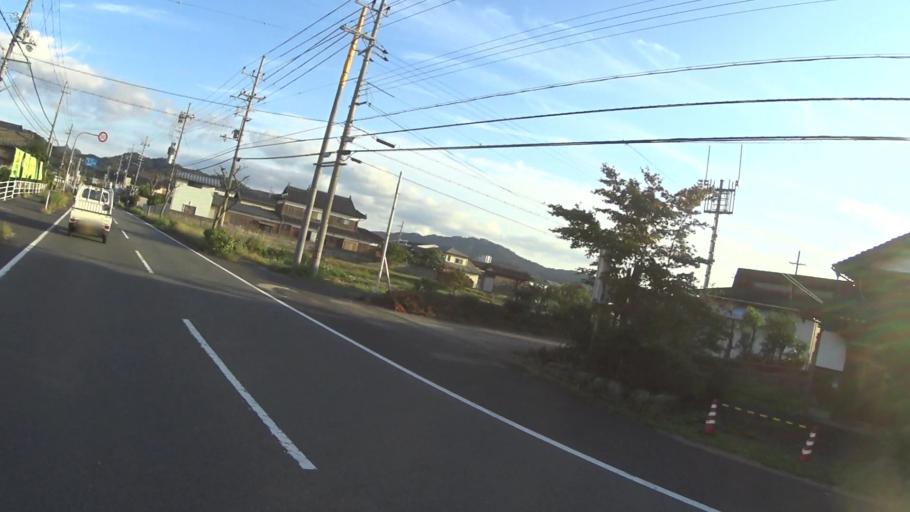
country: JP
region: Kyoto
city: Miyazu
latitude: 35.5863
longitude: 135.0973
